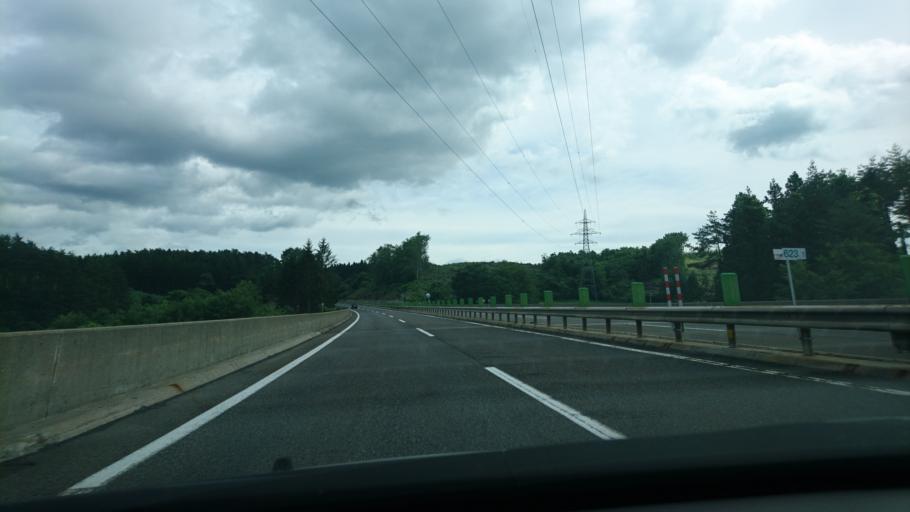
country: JP
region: Aomori
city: Hachinohe
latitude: 40.4240
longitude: 141.4393
